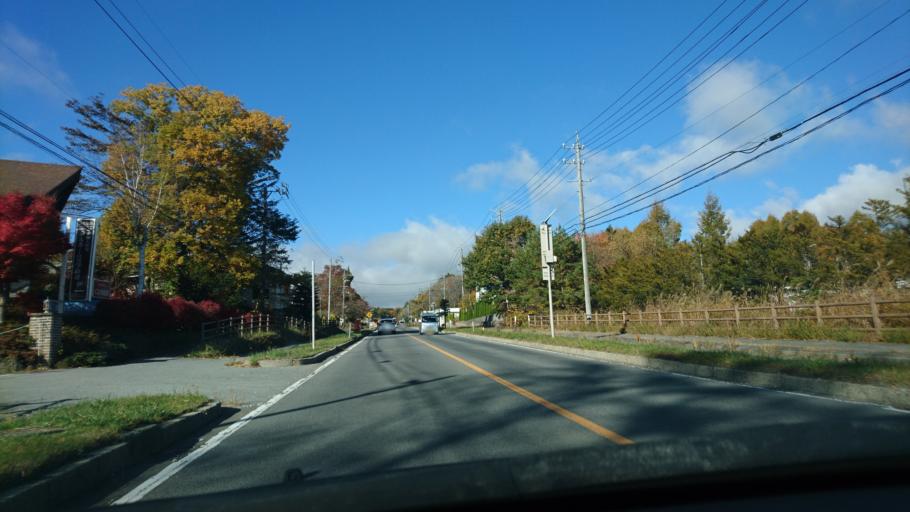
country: JP
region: Nagano
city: Komoro
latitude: 36.3392
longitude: 138.5820
